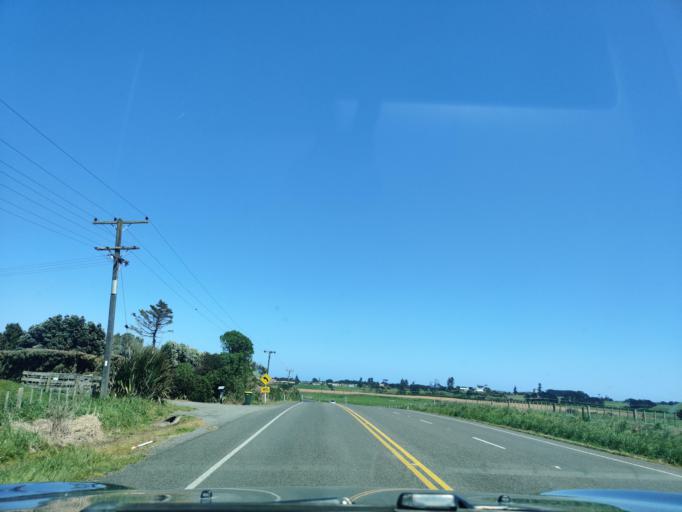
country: NZ
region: Taranaki
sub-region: South Taranaki District
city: Patea
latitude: -39.7461
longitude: 174.4873
